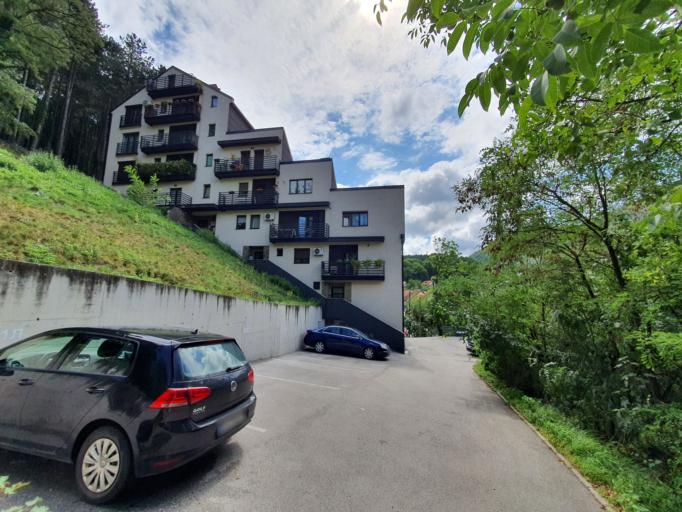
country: RS
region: Central Serbia
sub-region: Zlatiborski Okrug
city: Uzice
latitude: 43.8534
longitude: 19.8472
